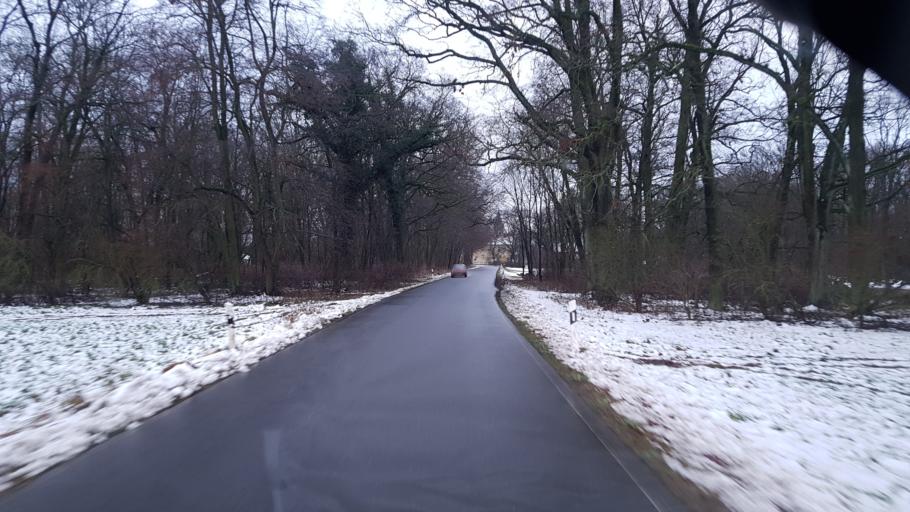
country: DE
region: Brandenburg
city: Luckau
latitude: 51.7978
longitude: 13.7347
